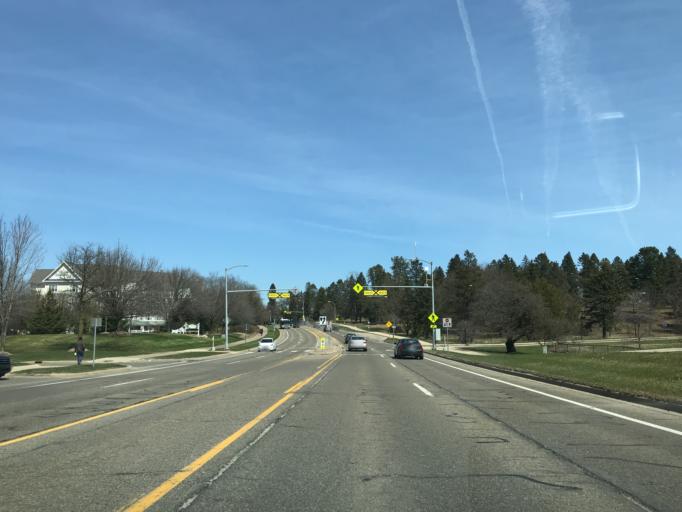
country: US
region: Michigan
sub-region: Washtenaw County
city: Ann Arbor
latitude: 42.2988
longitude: -83.7176
